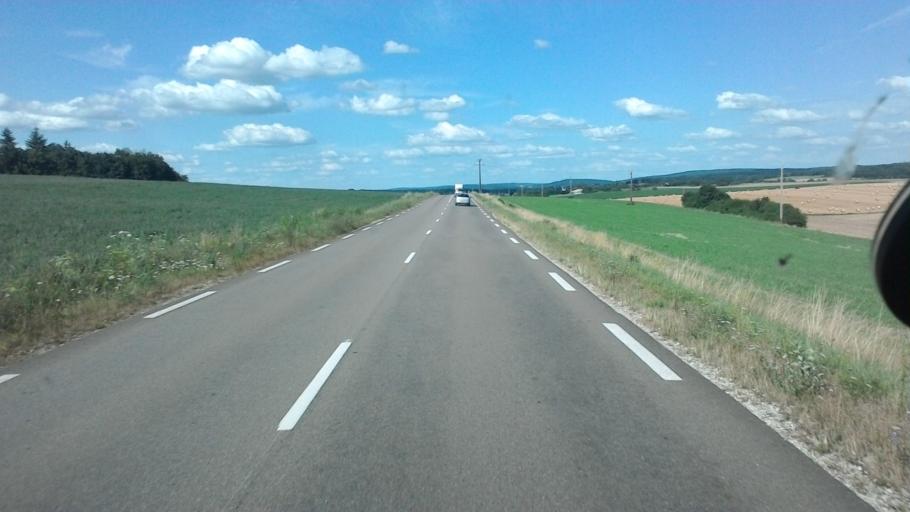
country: FR
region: Franche-Comte
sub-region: Departement de la Haute-Saone
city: Gy
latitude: 47.4738
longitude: 5.9270
